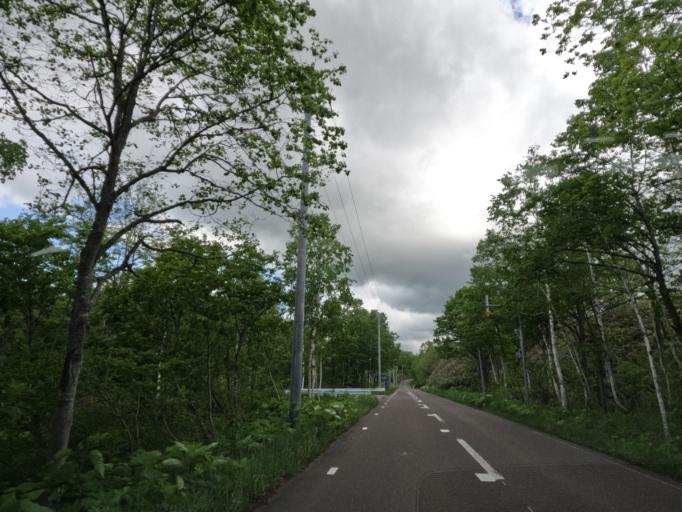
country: JP
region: Hokkaido
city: Tobetsu
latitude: 43.4589
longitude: 141.5932
